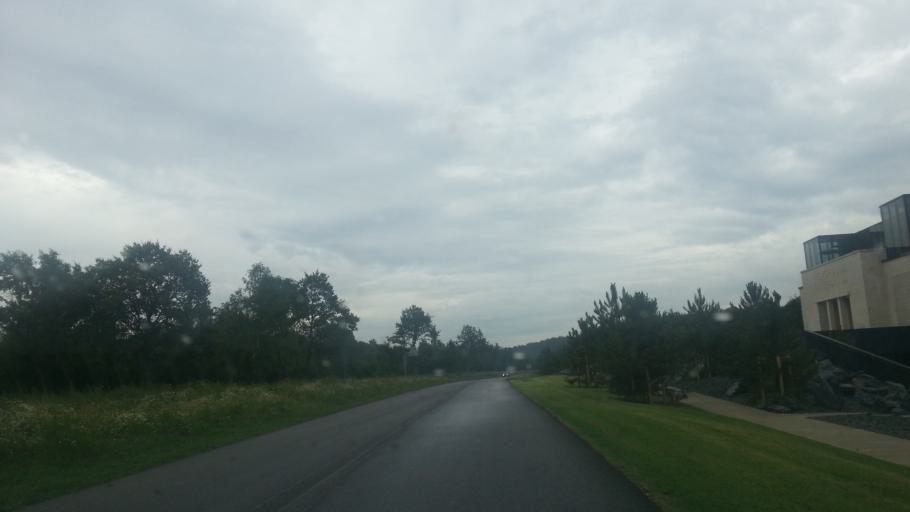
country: FR
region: Lorraine
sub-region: Departement de la Meuse
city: Verdun
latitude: 49.1957
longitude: 5.4332
